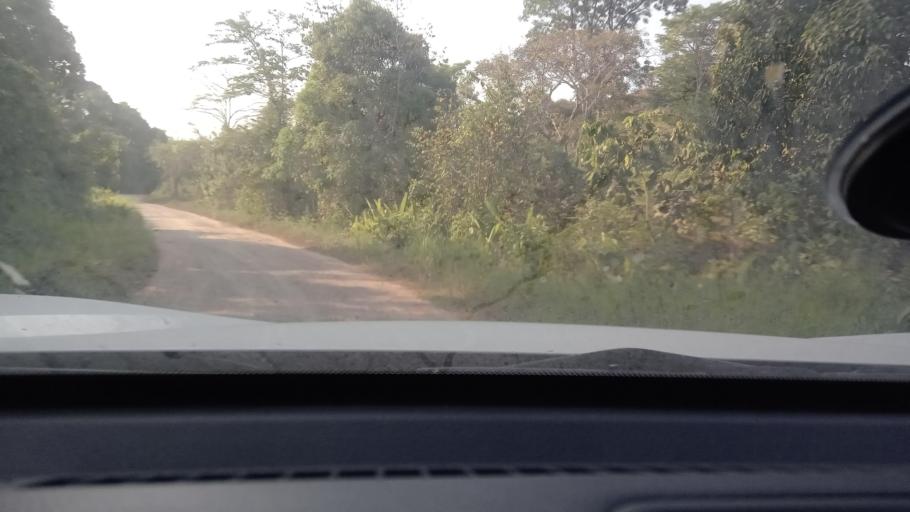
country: MX
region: Tabasco
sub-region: Huimanguillo
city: Francisco Rueda
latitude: 17.6728
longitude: -93.8671
